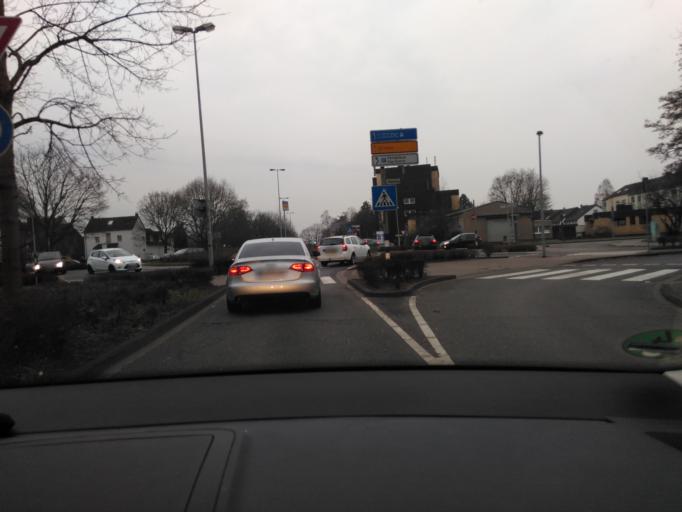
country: DE
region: North Rhine-Westphalia
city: Opladen
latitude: 51.0299
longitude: 7.0363
